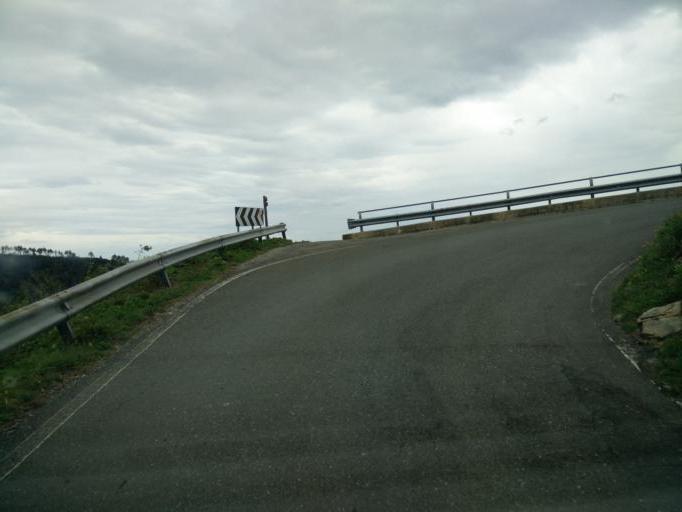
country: IT
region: Liguria
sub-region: Provincia di La Spezia
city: Riomaggiore
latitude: 44.1150
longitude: 9.7355
